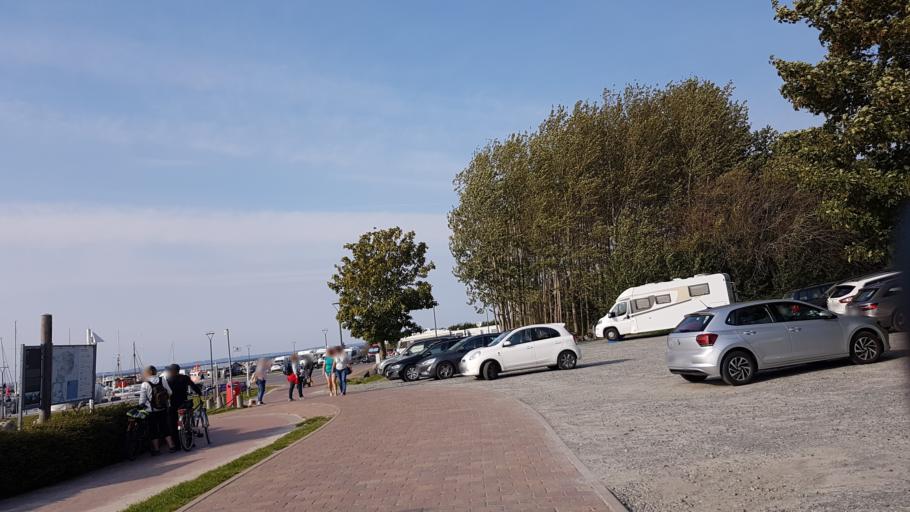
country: DE
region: Mecklenburg-Vorpommern
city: Glowe
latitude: 54.5729
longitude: 13.4700
